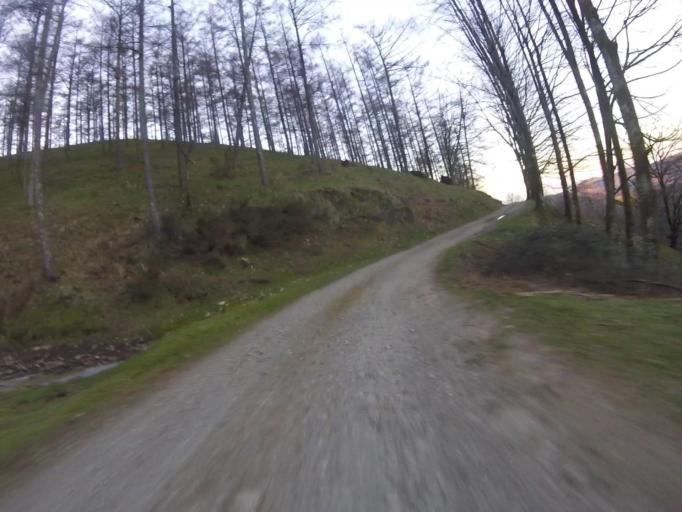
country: ES
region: Navarre
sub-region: Provincia de Navarra
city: Arano
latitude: 43.2561
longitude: -1.8263
